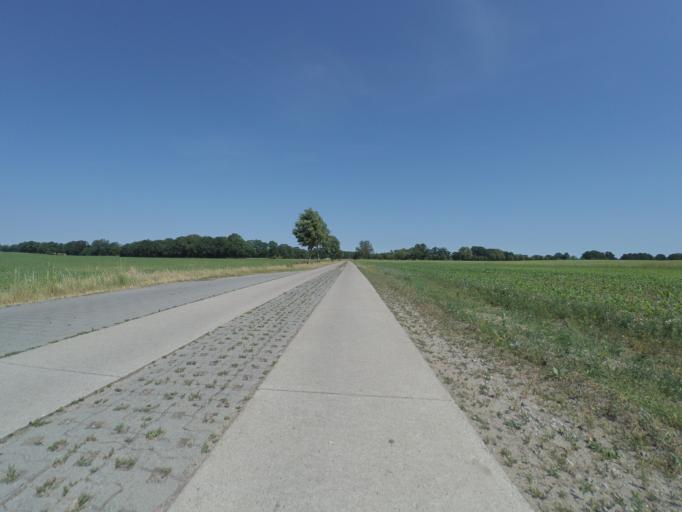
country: DE
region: Brandenburg
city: Heiligengrabe
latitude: 53.1889
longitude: 12.3107
